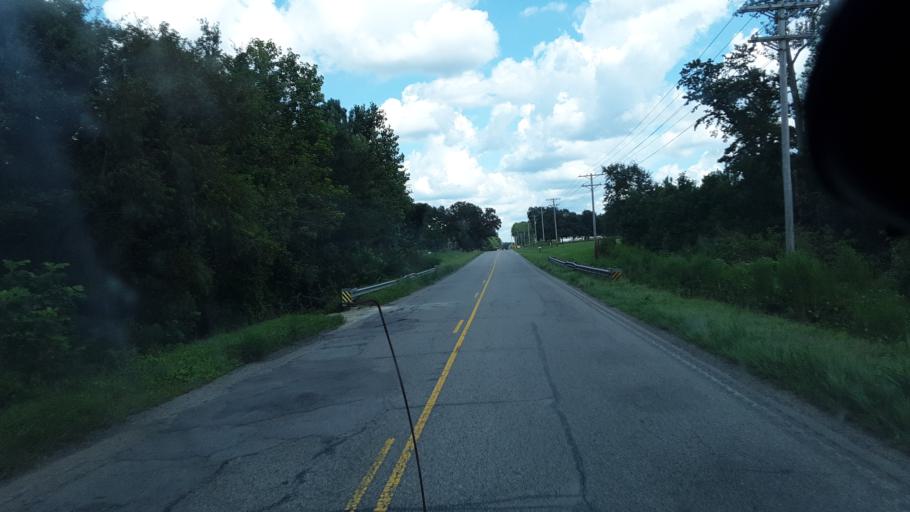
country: US
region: South Carolina
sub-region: Williamsburg County
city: Andrews
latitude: 33.5061
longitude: -79.5188
